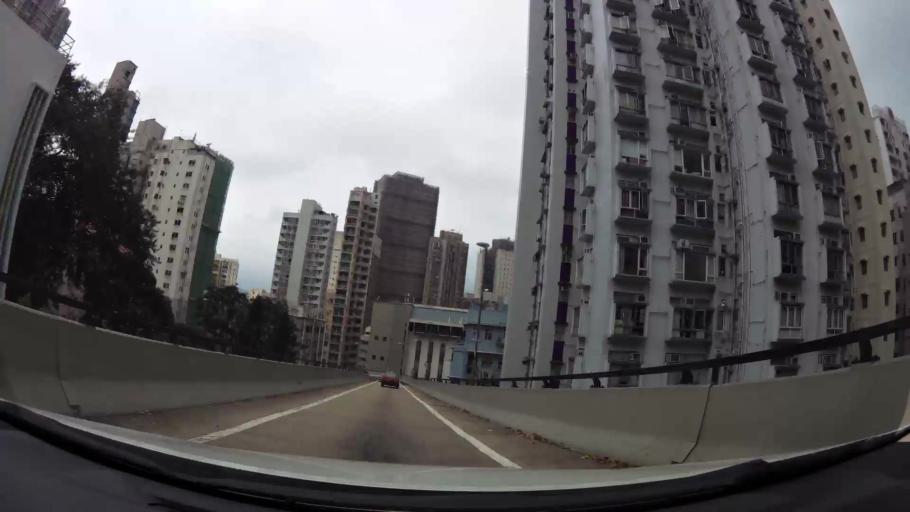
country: HK
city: Hong Kong
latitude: 22.2843
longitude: 114.1359
